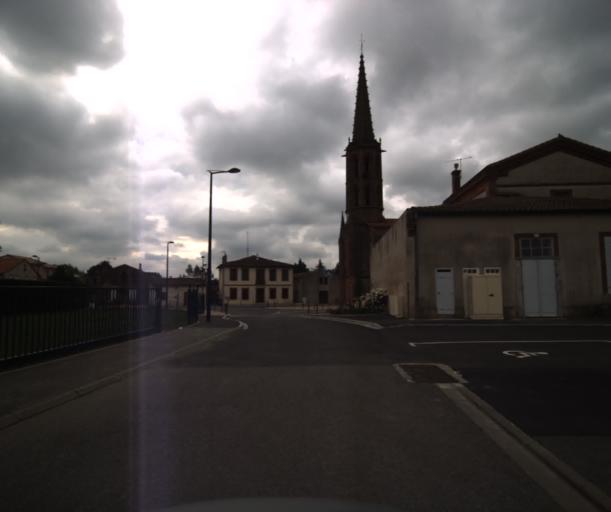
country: FR
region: Midi-Pyrenees
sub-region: Departement de la Haute-Garonne
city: Le Fauga
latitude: 43.4424
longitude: 1.2912
